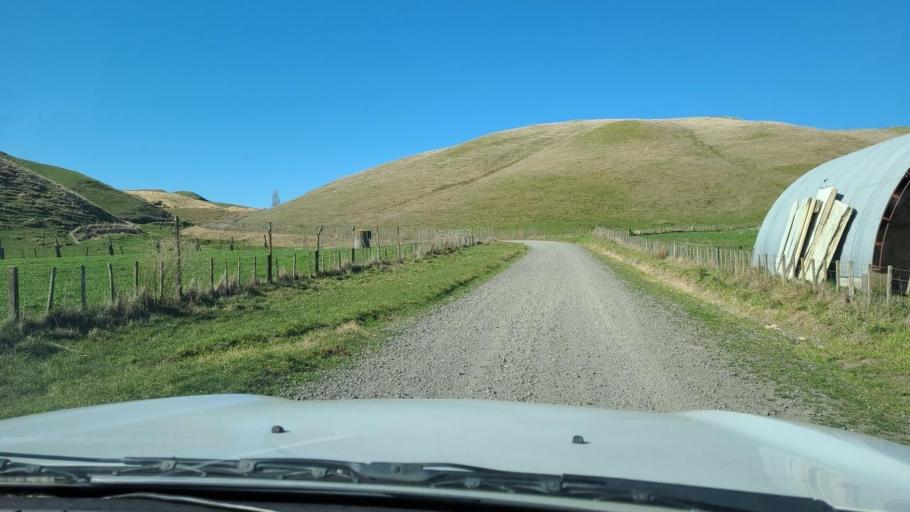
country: NZ
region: Hawke's Bay
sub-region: Hastings District
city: Hastings
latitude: -39.7617
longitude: 176.7984
